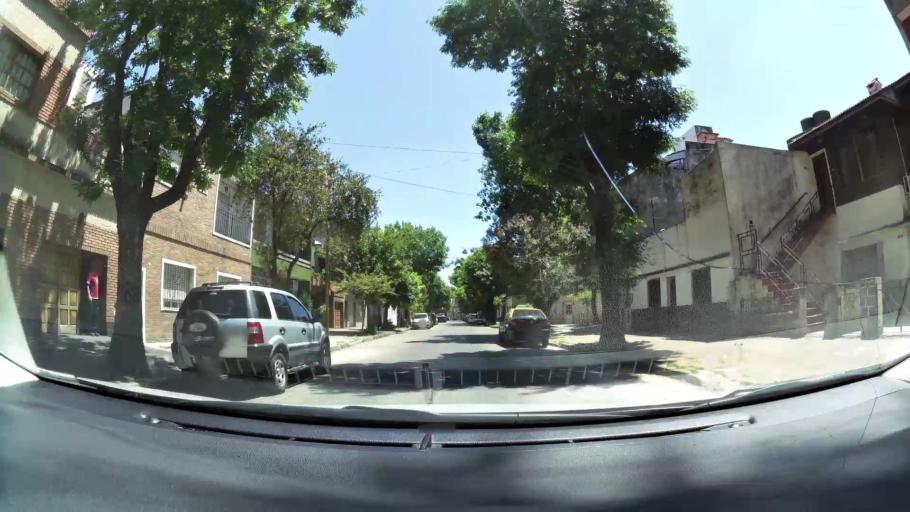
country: AR
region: Buenos Aires
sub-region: Partido de Avellaneda
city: Avellaneda
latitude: -34.6527
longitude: -58.3929
